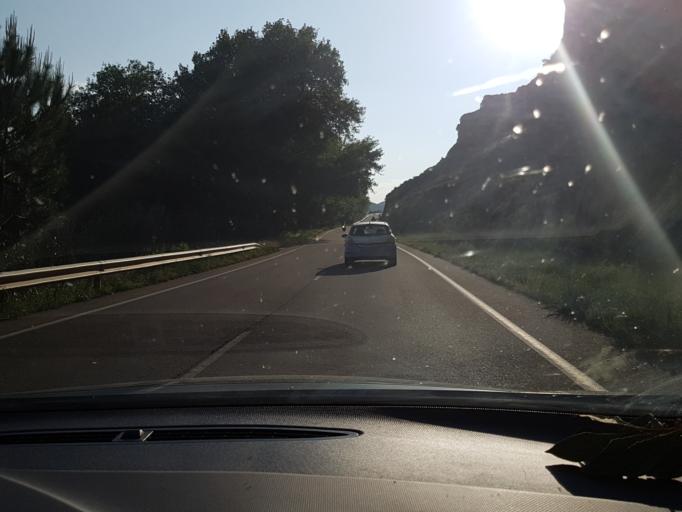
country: ES
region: La Rioja
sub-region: Provincia de La Rioja
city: Herce
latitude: 42.2133
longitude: -2.1464
